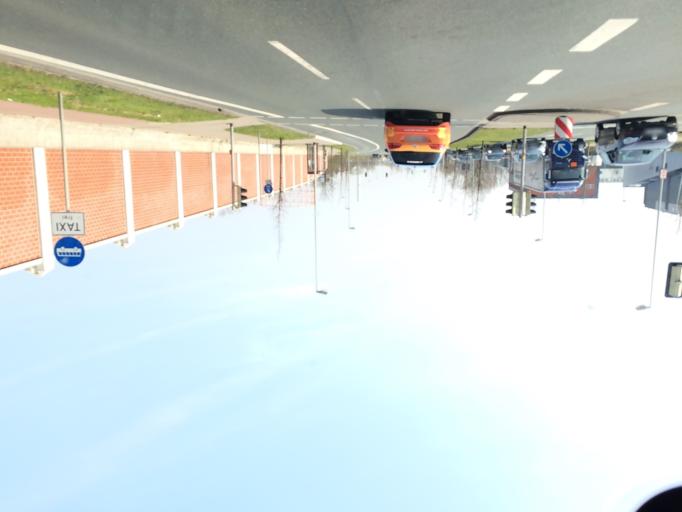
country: DE
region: North Rhine-Westphalia
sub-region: Regierungsbezirk Munster
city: Muenster
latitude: 51.9387
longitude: 7.6534
